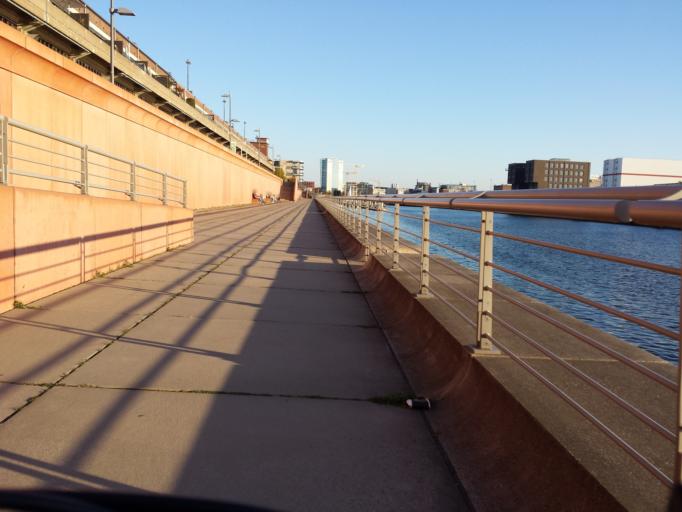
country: DE
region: Bremen
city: Bremen
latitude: 53.0905
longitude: 8.7731
